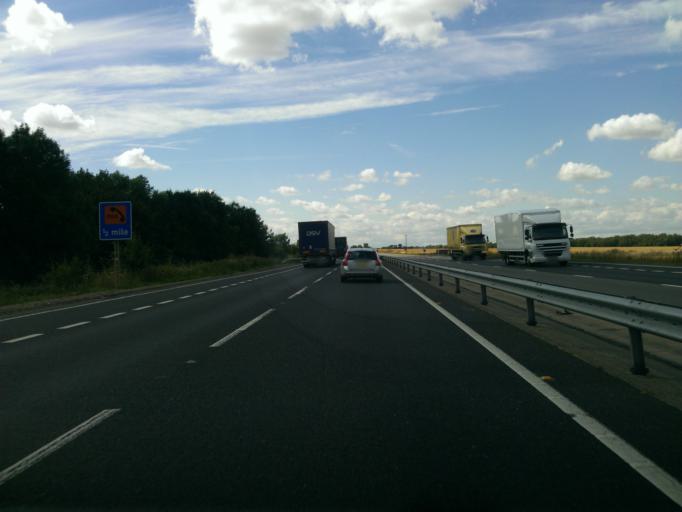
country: GB
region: England
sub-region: Bedford
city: Pertenhall
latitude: 52.3463
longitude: -0.3515
